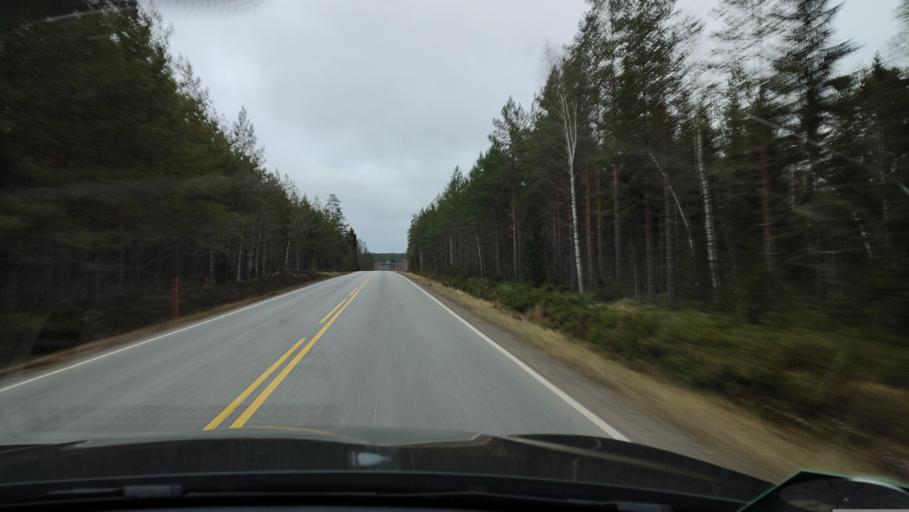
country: FI
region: Southern Ostrobothnia
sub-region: Suupohja
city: Karijoki
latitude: 62.2314
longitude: 21.7365
